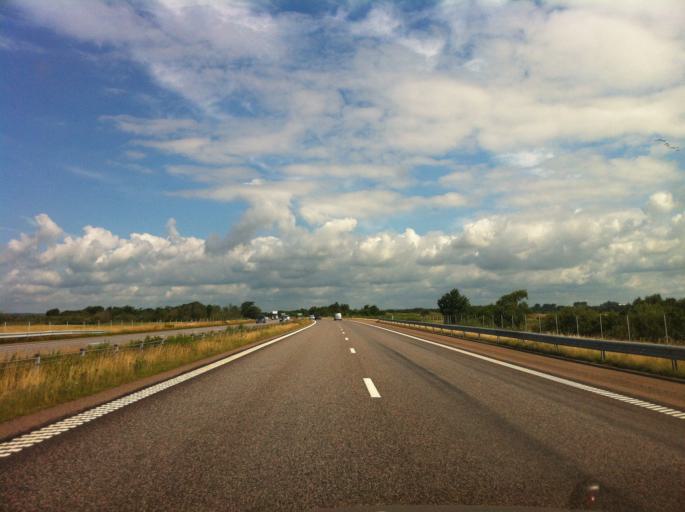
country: SE
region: Halland
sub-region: Halmstads Kommun
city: Troenninge
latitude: 56.6226
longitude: 12.9158
